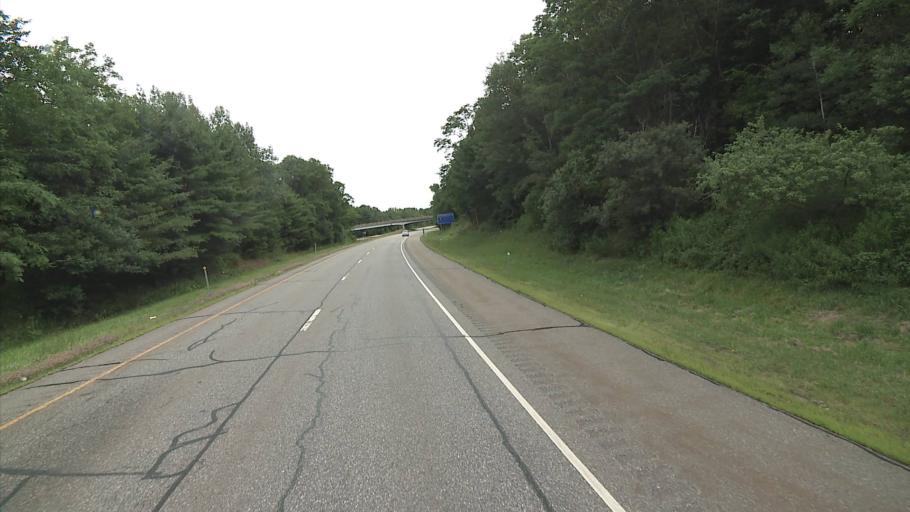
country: US
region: Connecticut
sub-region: Litchfield County
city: Winsted
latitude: 41.8644
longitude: -73.0831
